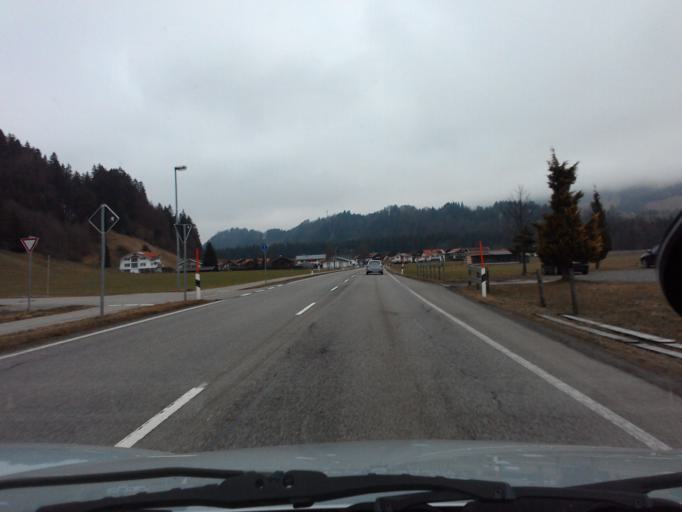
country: DE
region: Bavaria
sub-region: Swabia
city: Oberstdorf
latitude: 47.4330
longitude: 10.2710
